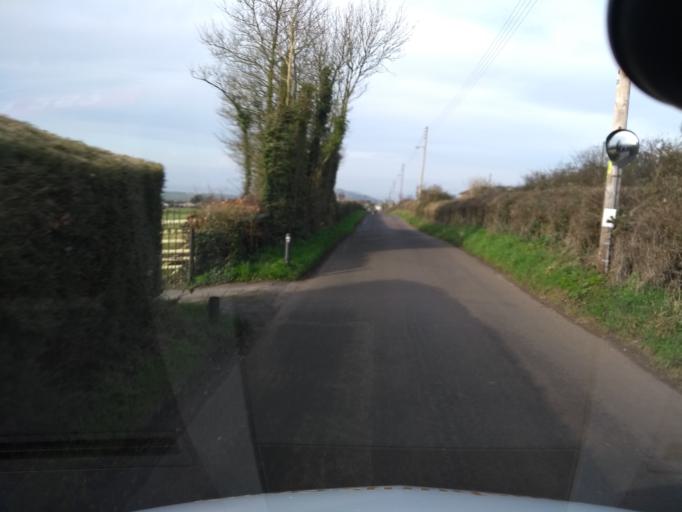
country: GB
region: England
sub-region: North Somerset
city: Bleadon
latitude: 51.3149
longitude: -2.9530
